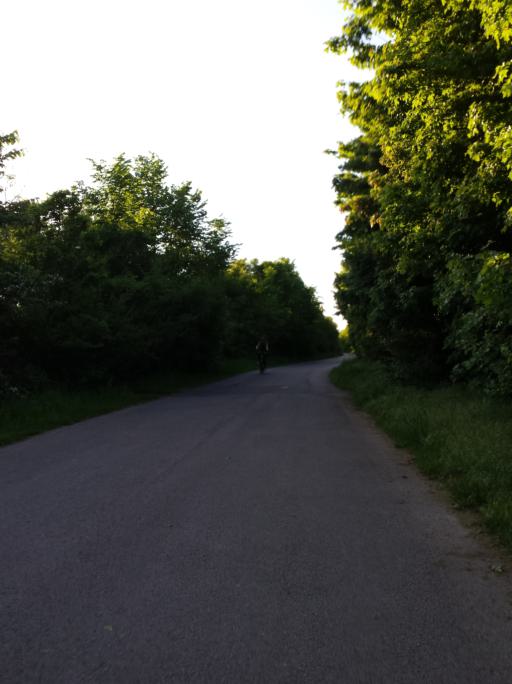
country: AT
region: Vienna
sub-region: Wien Stadt
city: Vienna
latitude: 48.2118
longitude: 16.4315
